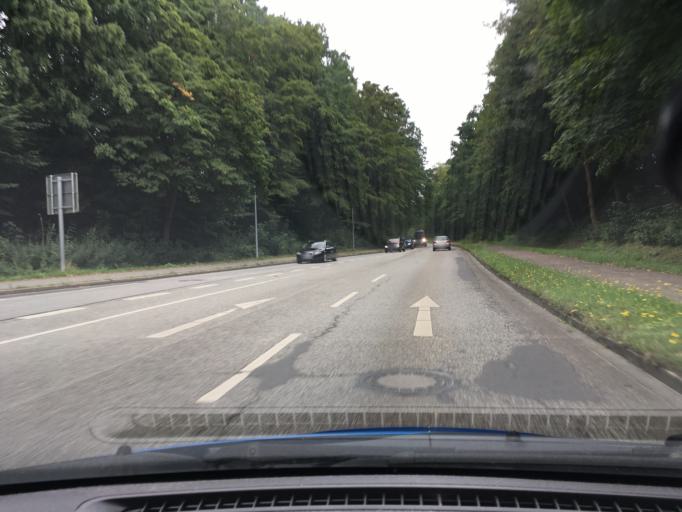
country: DE
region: Schleswig-Holstein
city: Geesthacht
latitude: 53.4352
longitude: 10.3865
